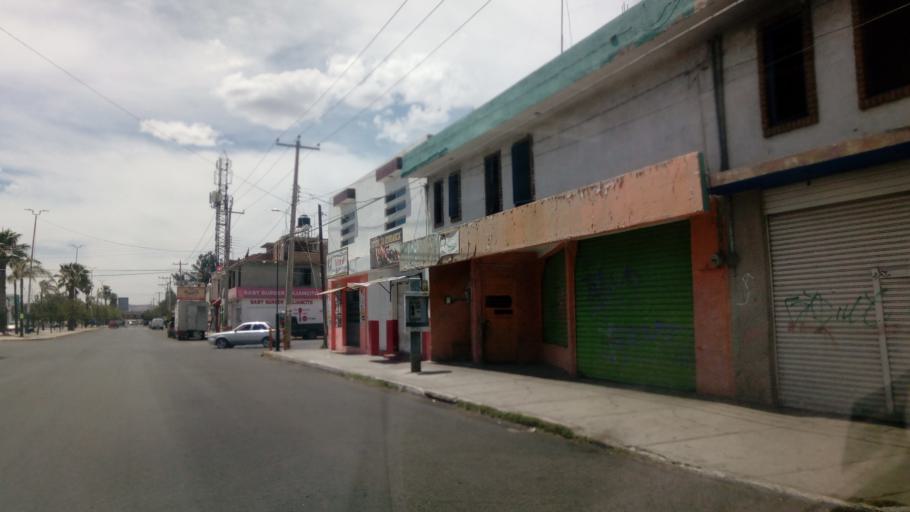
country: MX
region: Durango
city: Victoria de Durango
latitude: 23.9970
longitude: -104.6717
